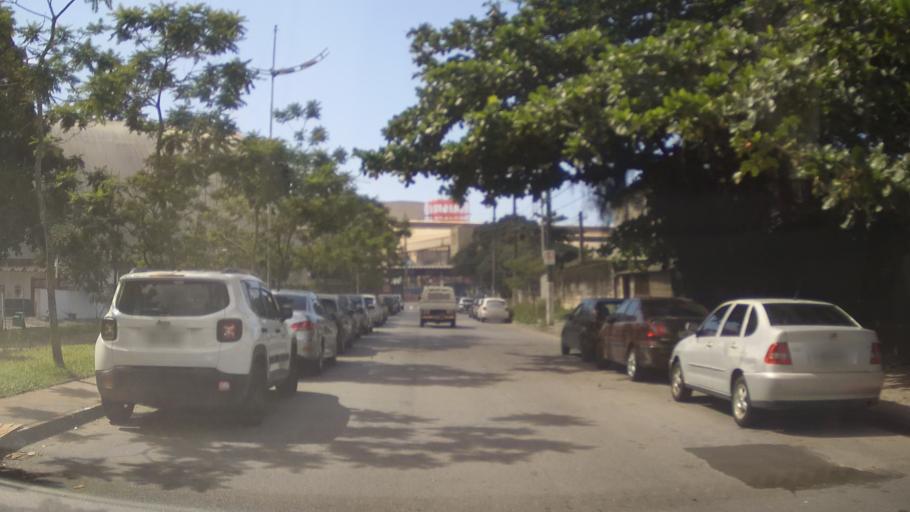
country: BR
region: Sao Paulo
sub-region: Guaruja
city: Guaruja
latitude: -23.9786
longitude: -46.2950
